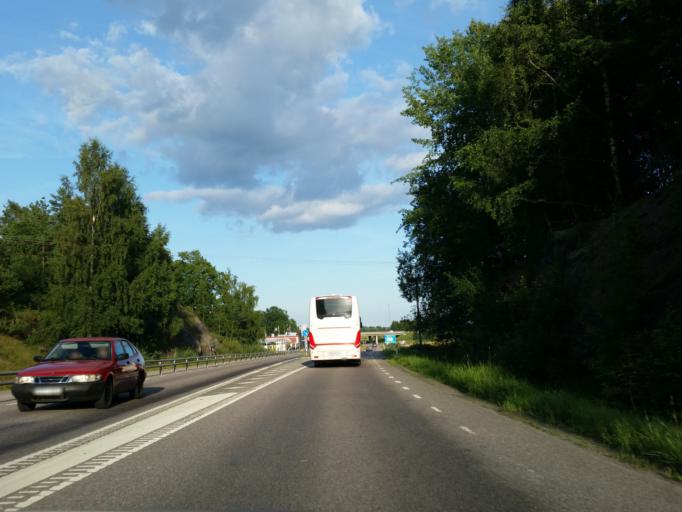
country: SE
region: Stockholm
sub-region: Sodertalje Kommun
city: Pershagen
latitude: 59.0872
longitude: 17.5898
